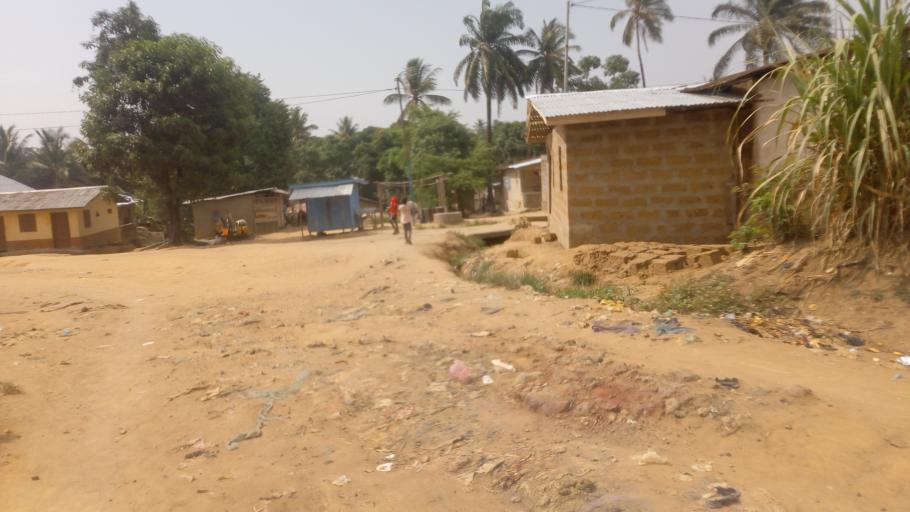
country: SL
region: Western Area
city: Waterloo
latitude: 8.3282
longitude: -13.0655
